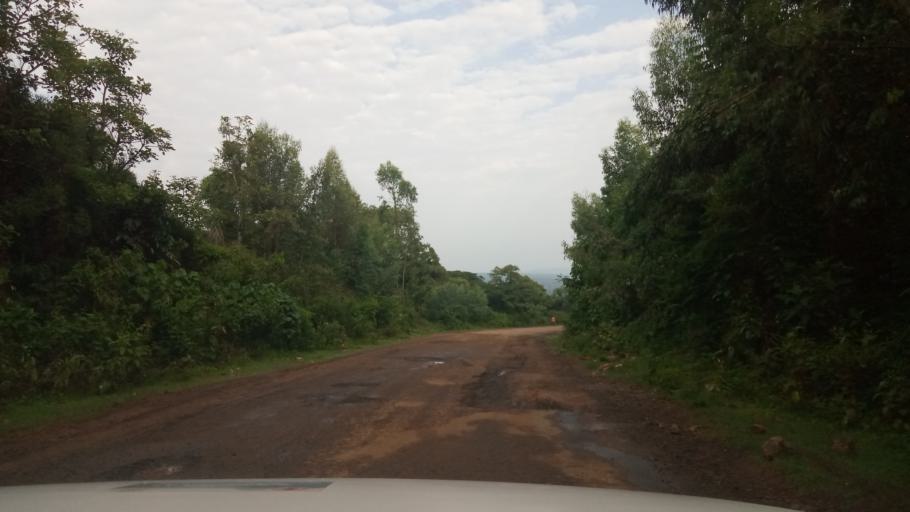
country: ET
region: Oromiya
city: Agaro
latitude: 7.7974
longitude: 36.7188
